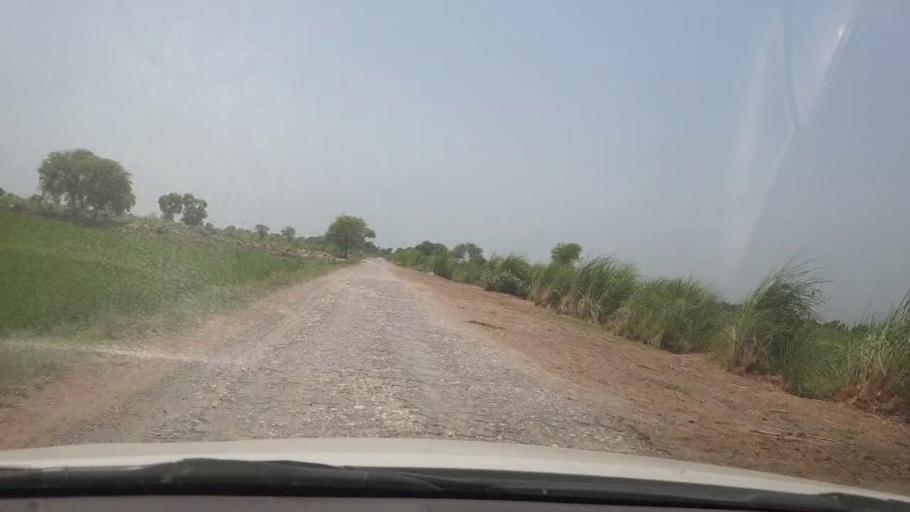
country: PK
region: Sindh
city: Shikarpur
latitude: 28.0865
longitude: 68.5608
